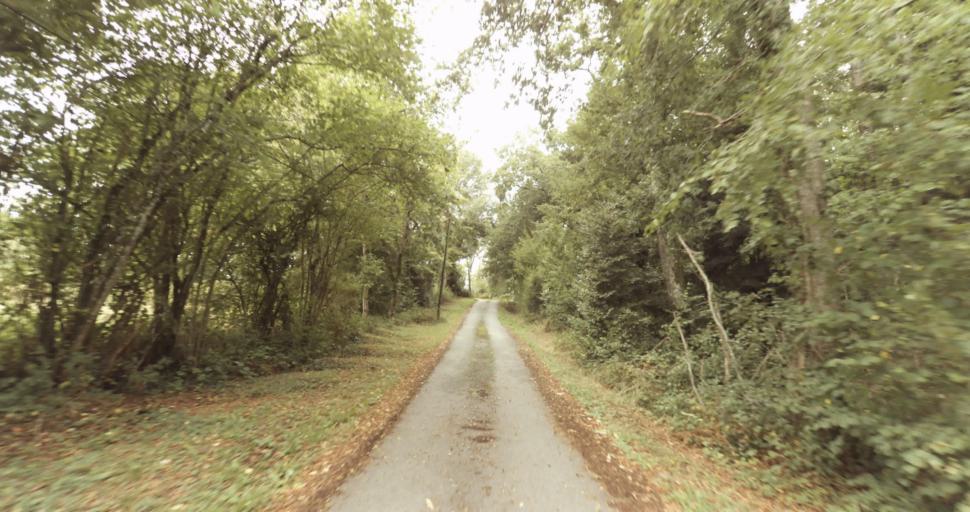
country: FR
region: Lower Normandy
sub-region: Departement de l'Orne
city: Sainte-Gauburge-Sainte-Colombe
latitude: 48.7522
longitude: 0.3884
